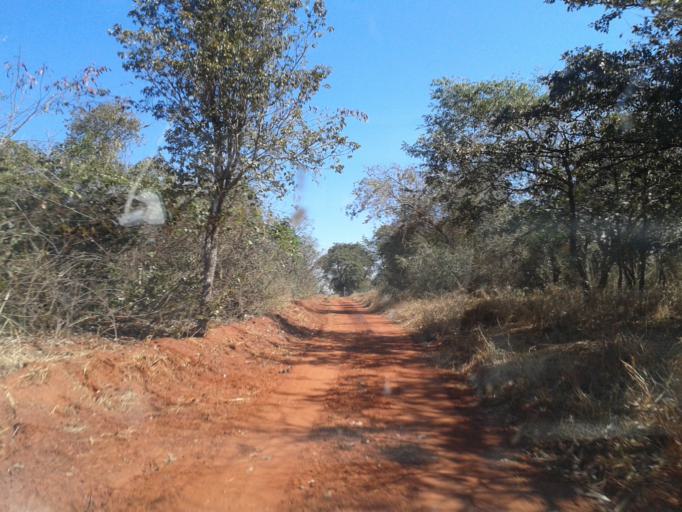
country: BR
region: Minas Gerais
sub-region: Santa Vitoria
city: Santa Vitoria
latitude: -19.0179
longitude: -50.4490
